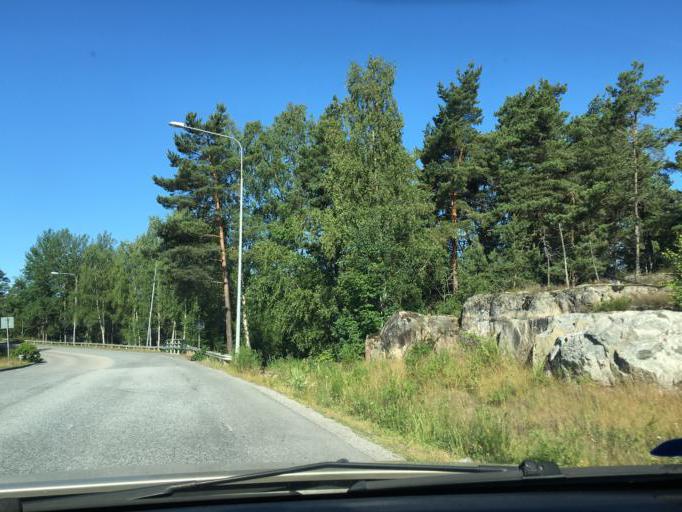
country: SE
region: Stockholm
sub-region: Sodertalje Kommun
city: Soedertaelje
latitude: 59.1963
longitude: 17.6639
